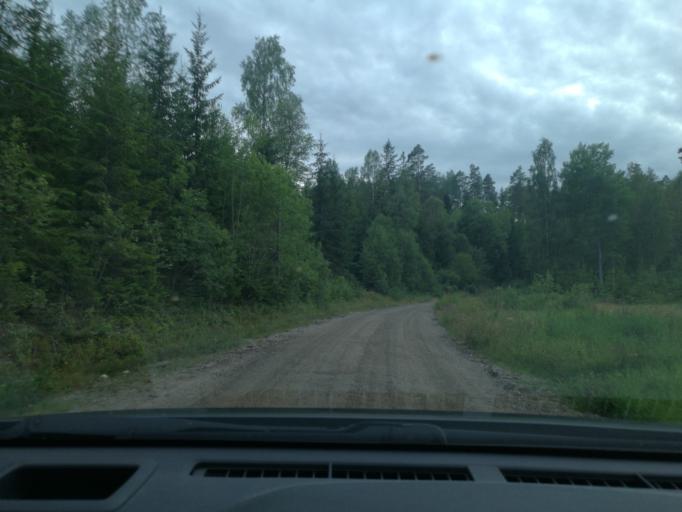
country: SE
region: OEstergoetland
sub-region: Norrkopings Kommun
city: Svartinge
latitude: 58.8118
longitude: 15.9584
